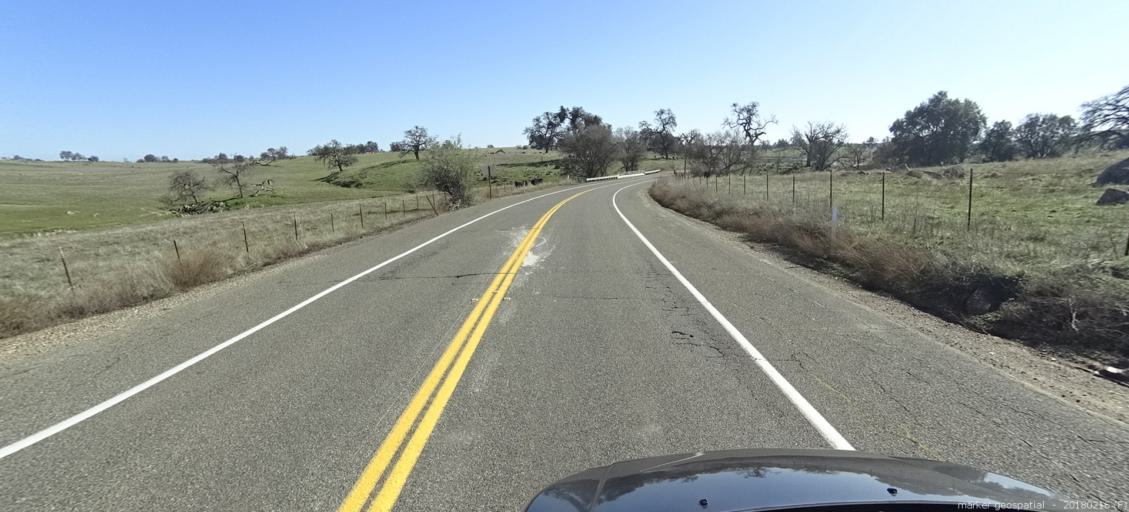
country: US
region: California
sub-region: Sacramento County
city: Folsom
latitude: 38.5942
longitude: -121.1297
